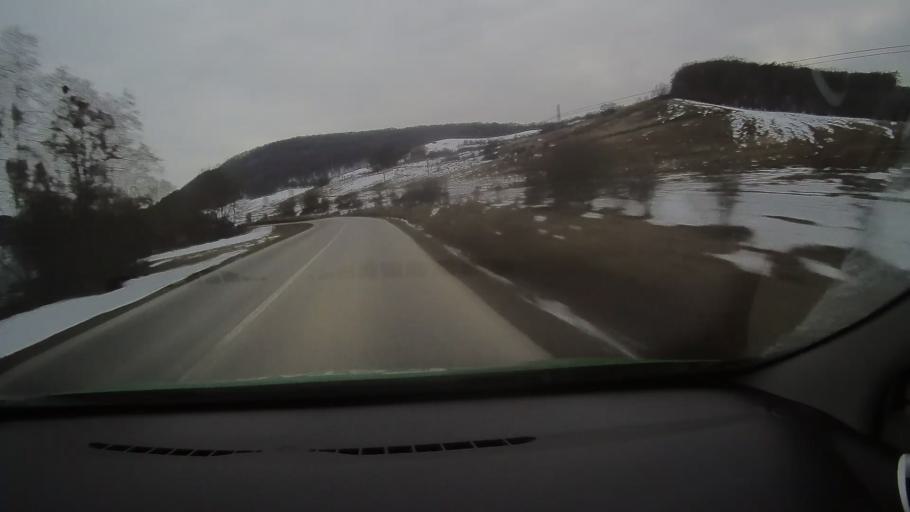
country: RO
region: Harghita
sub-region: Comuna Mugeni
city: Mugeni
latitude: 46.2297
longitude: 25.2394
